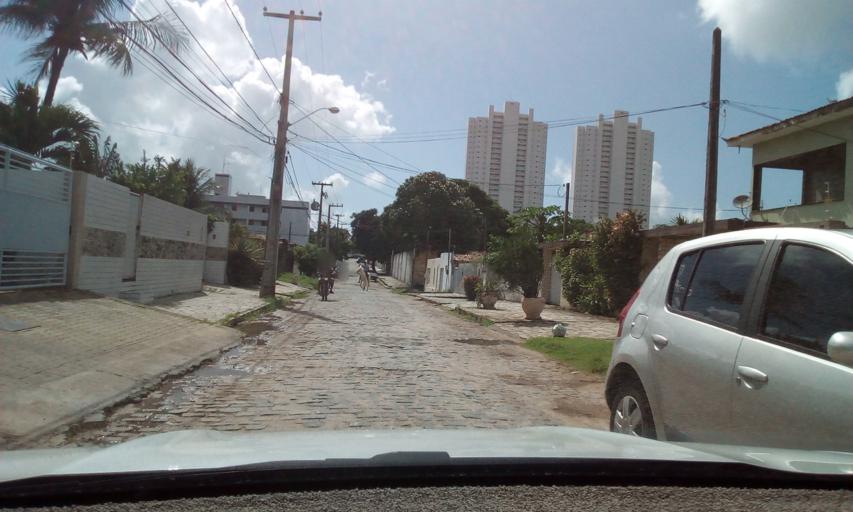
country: BR
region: Paraiba
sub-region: Joao Pessoa
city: Joao Pessoa
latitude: -7.1383
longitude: -34.8310
